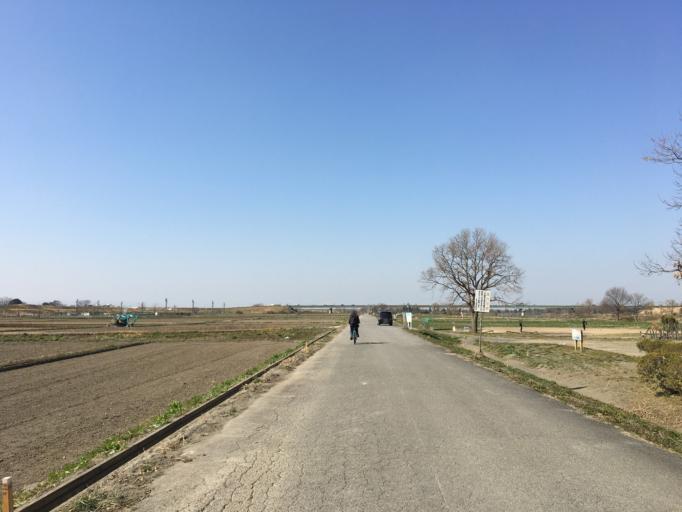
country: JP
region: Saitama
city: Shiki
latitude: 35.8488
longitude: 139.5941
